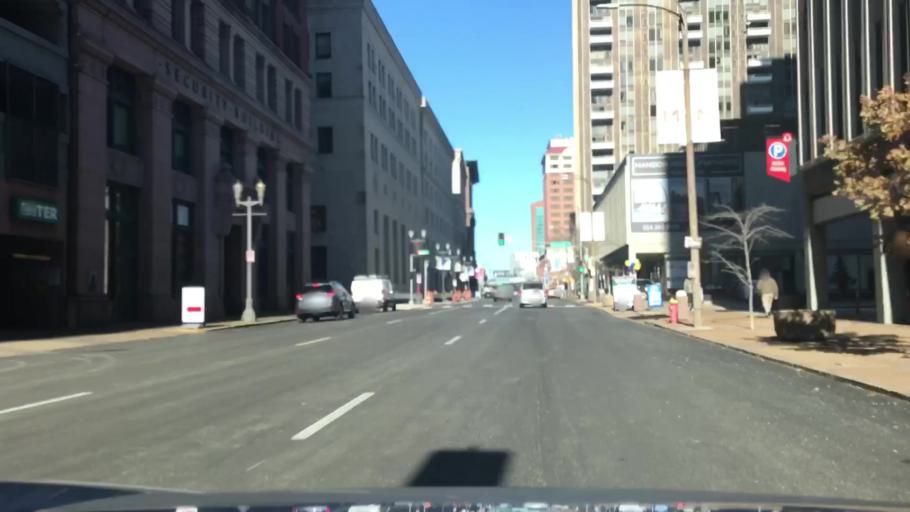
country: US
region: Missouri
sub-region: City of Saint Louis
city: St. Louis
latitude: 38.6277
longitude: -90.1878
